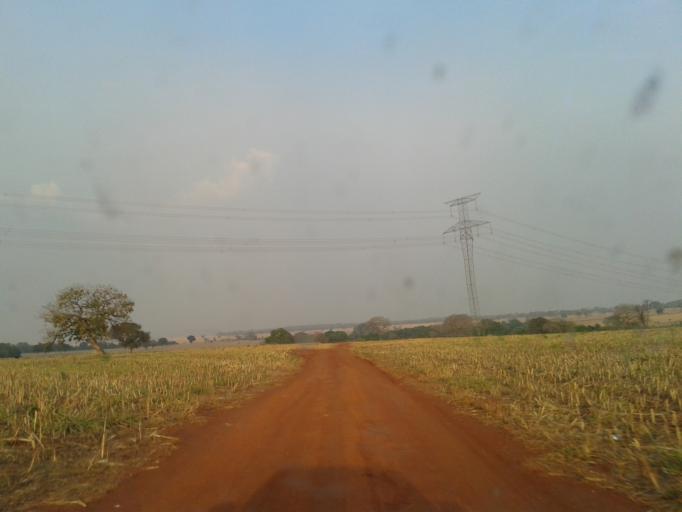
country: BR
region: Minas Gerais
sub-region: Capinopolis
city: Capinopolis
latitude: -18.8073
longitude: -49.7388
